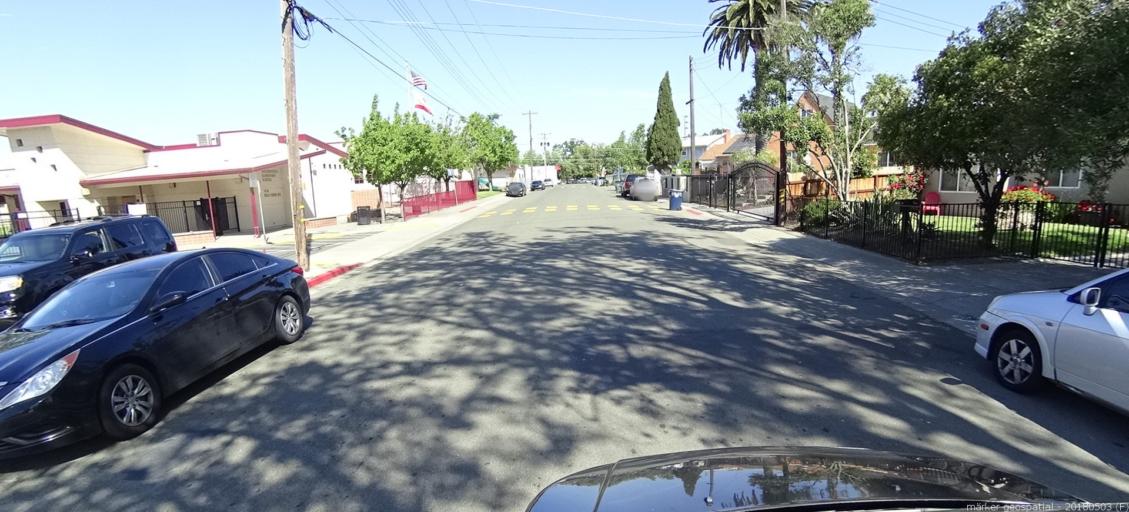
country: US
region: California
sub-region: Sacramento County
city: Arden-Arcade
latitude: 38.6225
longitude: -121.4331
